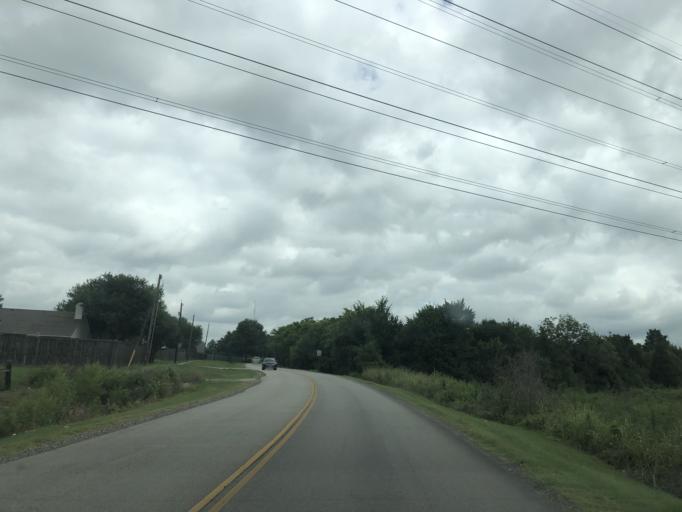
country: US
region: Texas
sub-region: Dallas County
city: Sunnyvale
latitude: 32.8342
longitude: -96.5599
